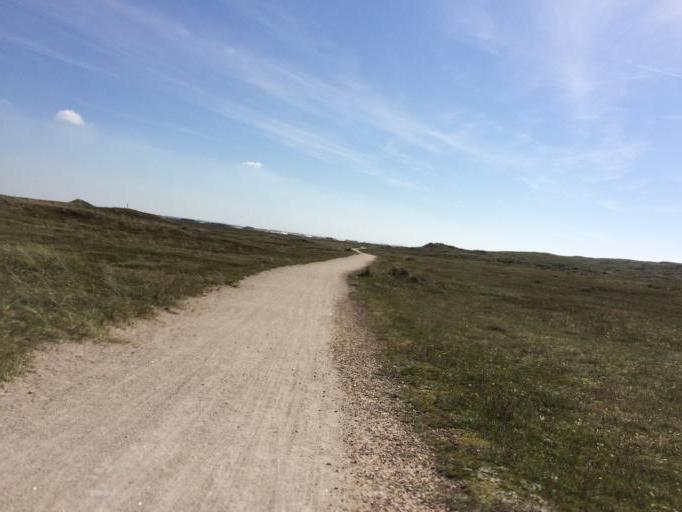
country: DK
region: Central Jutland
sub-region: Ringkobing-Skjern Kommune
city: Hvide Sande
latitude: 55.8576
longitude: 8.1637
